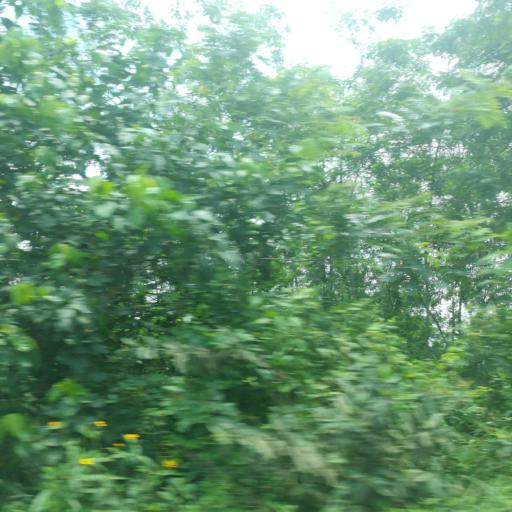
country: NG
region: Lagos
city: Ejirin
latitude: 6.6784
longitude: 3.7998
